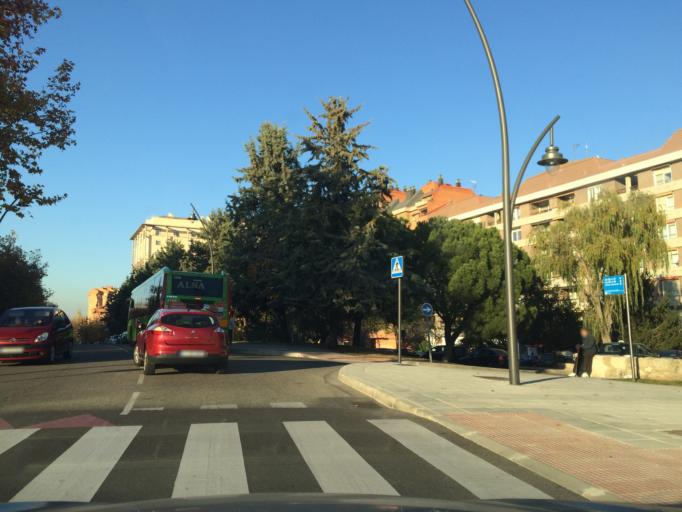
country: ES
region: Madrid
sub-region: Provincia de Madrid
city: Tres Cantos
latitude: 40.5936
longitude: -3.7031
